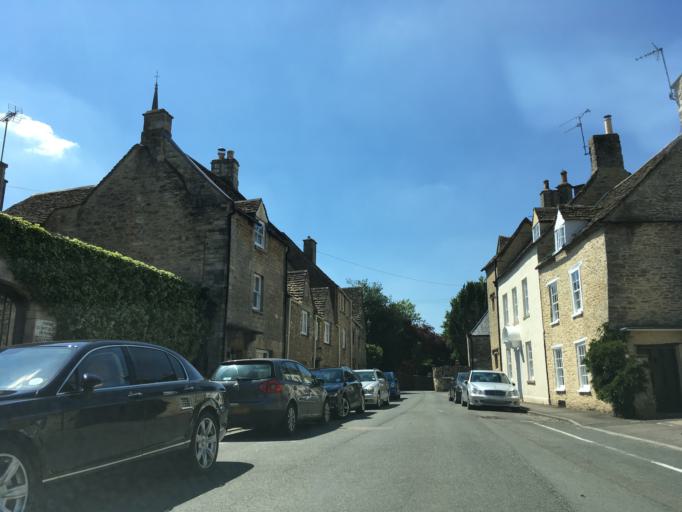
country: GB
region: England
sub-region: Gloucestershire
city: Tetbury
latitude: 51.6358
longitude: -2.1586
